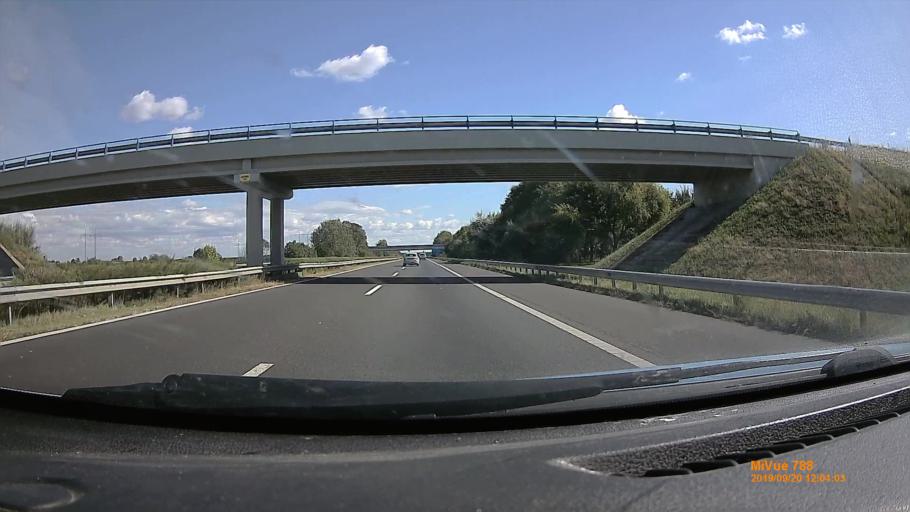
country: HU
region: Heves
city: Fuzesabony
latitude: 47.7307
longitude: 20.3991
